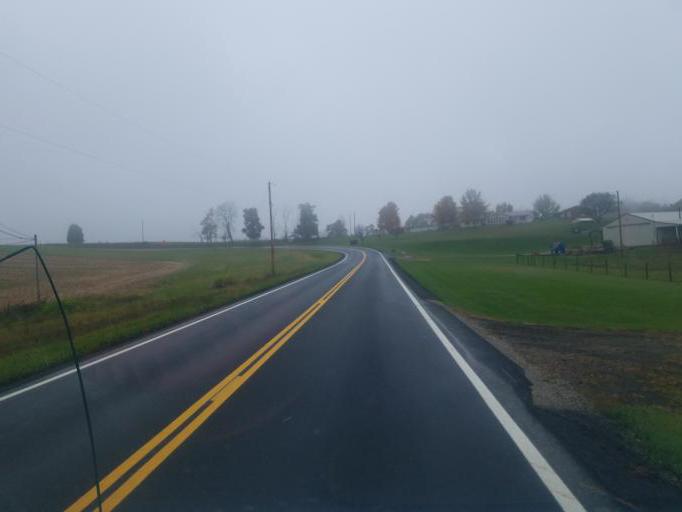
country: US
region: Ohio
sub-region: Morgan County
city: McConnelsville
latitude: 39.5671
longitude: -81.8365
